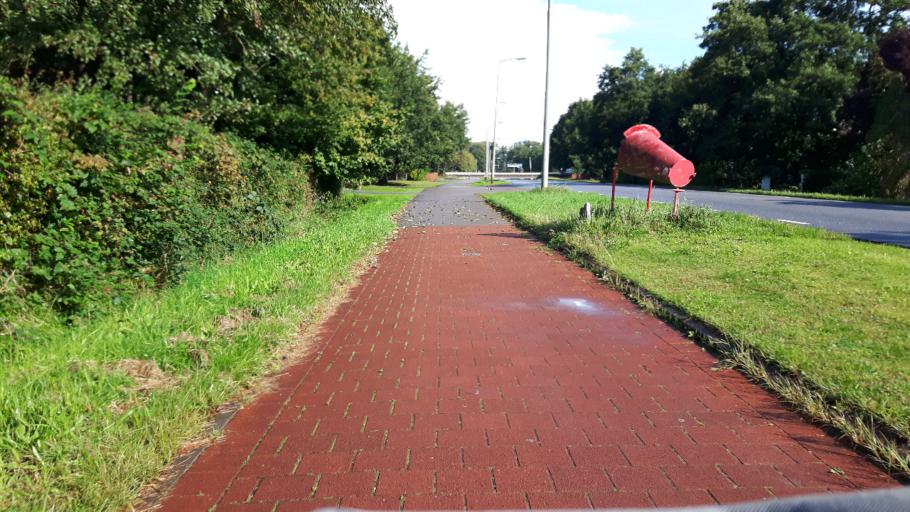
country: NL
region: Friesland
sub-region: Gemeente Smallingerland
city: Drachten
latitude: 53.0911
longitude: 6.0994
